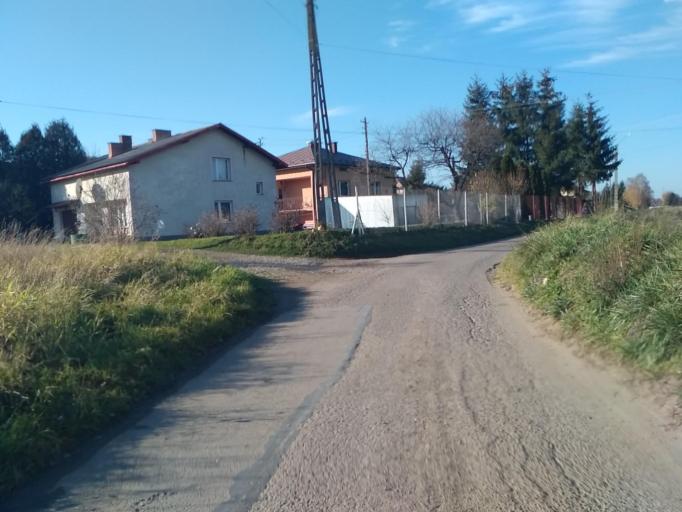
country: PL
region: Subcarpathian Voivodeship
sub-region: Powiat brzozowski
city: Humniska
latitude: 49.6752
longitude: 22.0472
